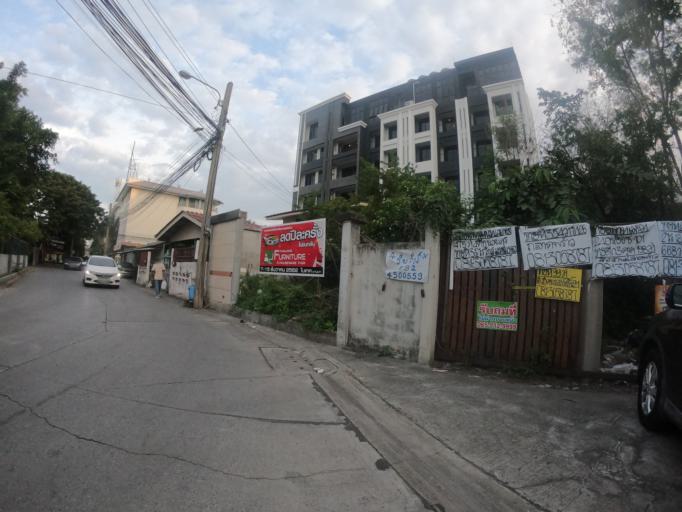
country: TH
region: Bangkok
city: Lat Phrao
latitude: 13.8321
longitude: 100.6206
